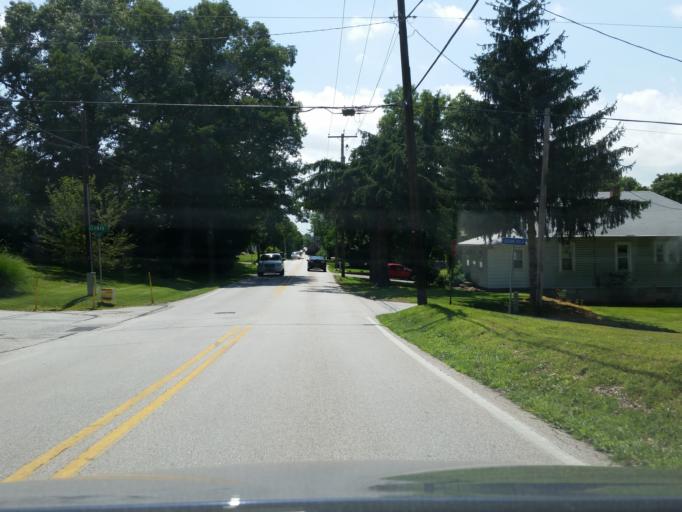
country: US
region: Pennsylvania
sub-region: York County
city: Shiloh
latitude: 39.9826
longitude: -76.7972
